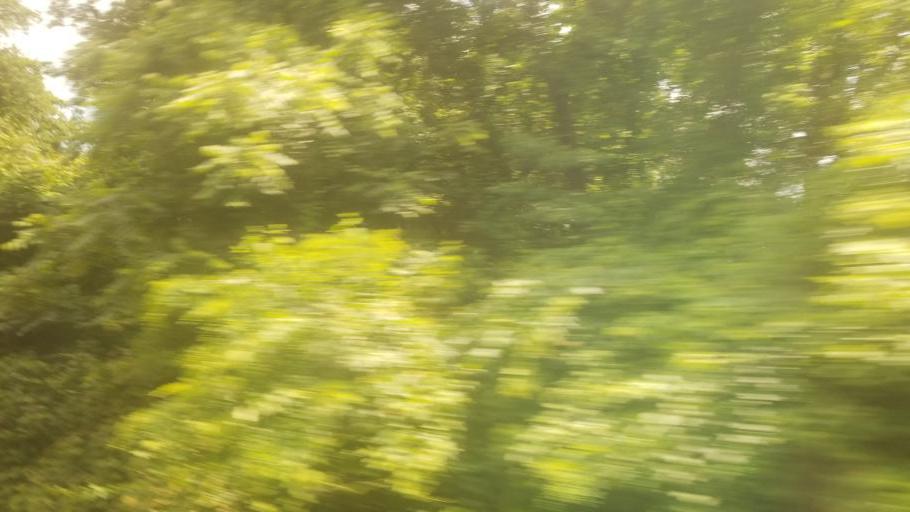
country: US
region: Maryland
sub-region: Montgomery County
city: Poolesville
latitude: 39.2200
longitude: -77.4155
